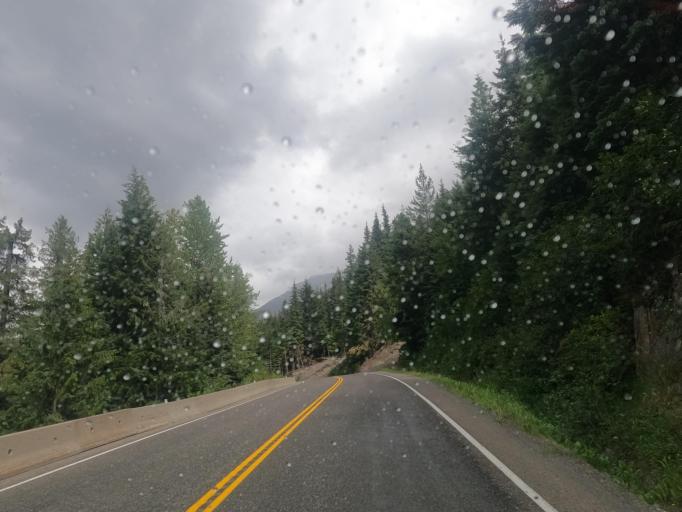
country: CA
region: British Columbia
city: Lillooet
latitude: 50.4738
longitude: -122.2281
